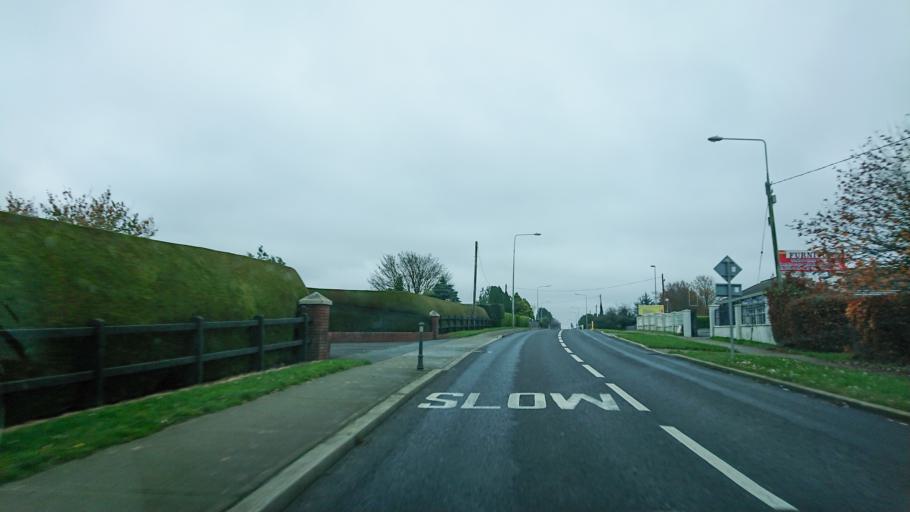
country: IE
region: Leinster
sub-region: Kilkenny
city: Mooncoin
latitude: 52.2911
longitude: -7.2484
